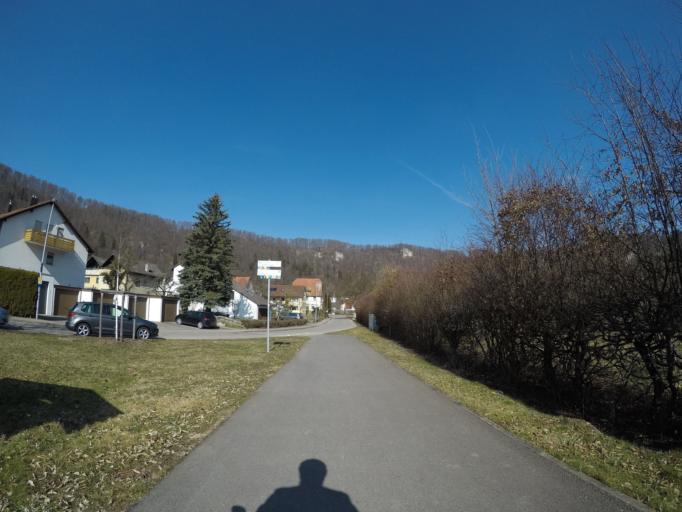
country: DE
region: Baden-Wuerttemberg
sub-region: Tuebingen Region
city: Blaubeuren
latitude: 48.4011
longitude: 9.7675
